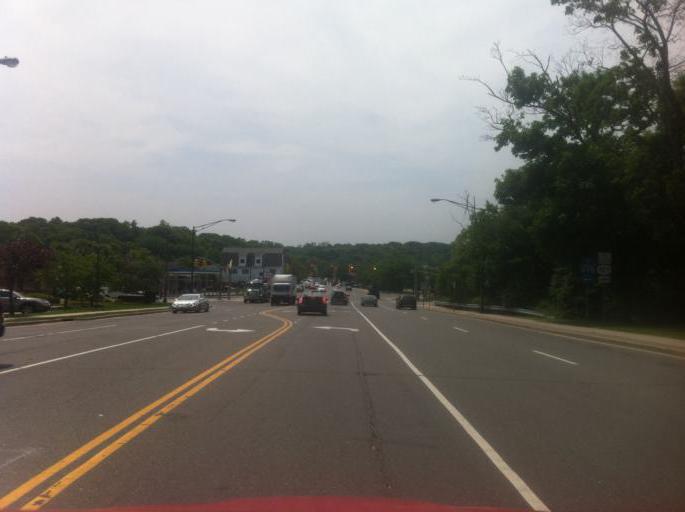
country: US
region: New York
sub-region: Nassau County
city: Glen Cove
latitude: 40.8647
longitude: -73.6330
